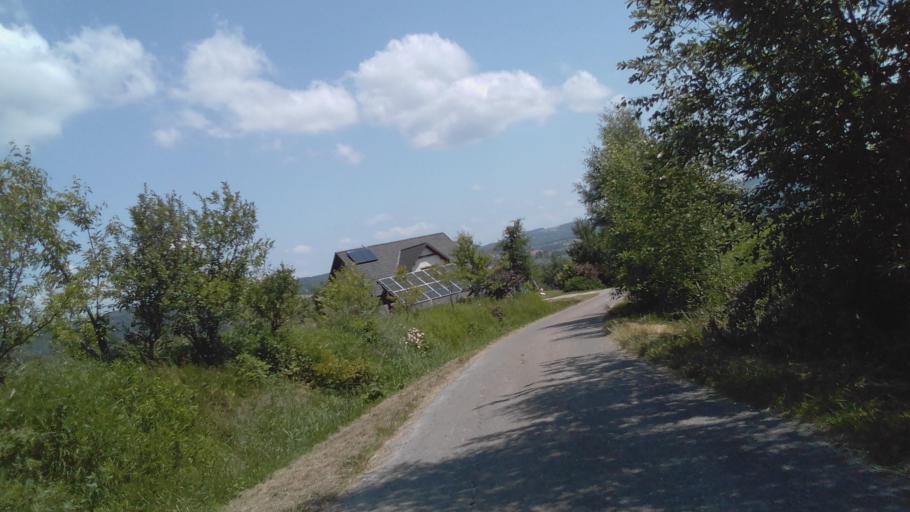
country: PL
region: Subcarpathian Voivodeship
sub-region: Powiat strzyzowski
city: Strzyzow
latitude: 49.8616
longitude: 21.7608
